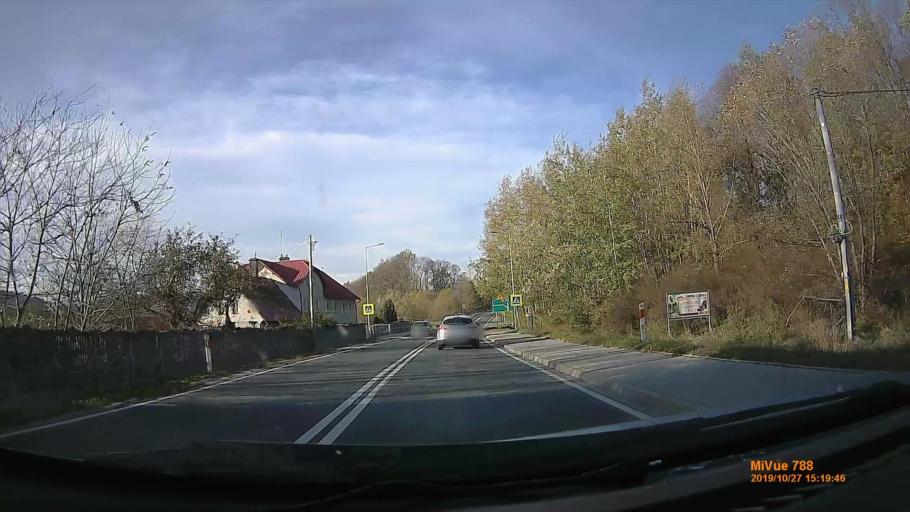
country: PL
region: Lower Silesian Voivodeship
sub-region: Powiat klodzki
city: Bystrzyca Klodzka
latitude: 50.2764
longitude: 16.6500
